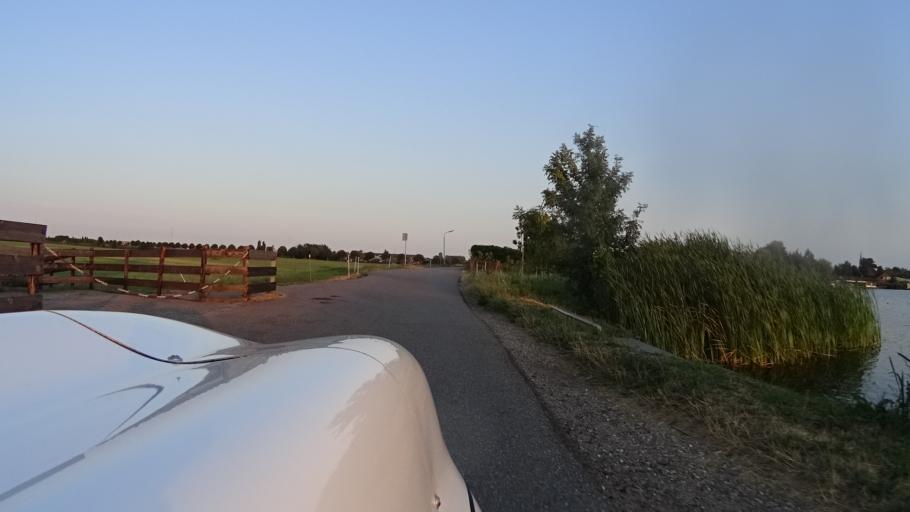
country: NL
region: South Holland
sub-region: Gemeente Kaag en Braassem
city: Oude Wetering
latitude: 52.1993
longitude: 4.5848
